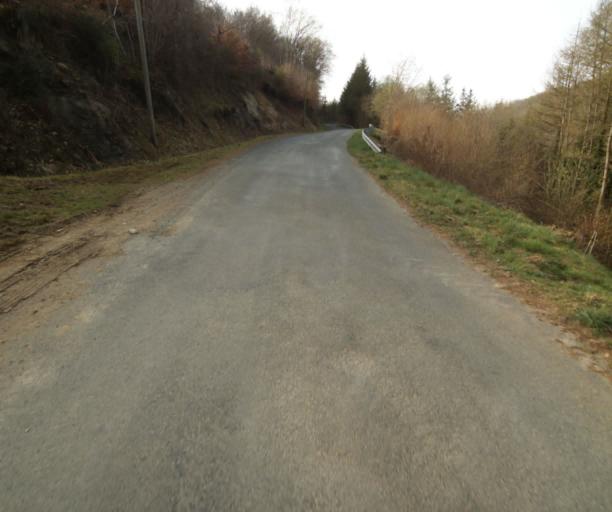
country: FR
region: Limousin
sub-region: Departement de la Correze
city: Correze
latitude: 45.4267
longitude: 1.8022
